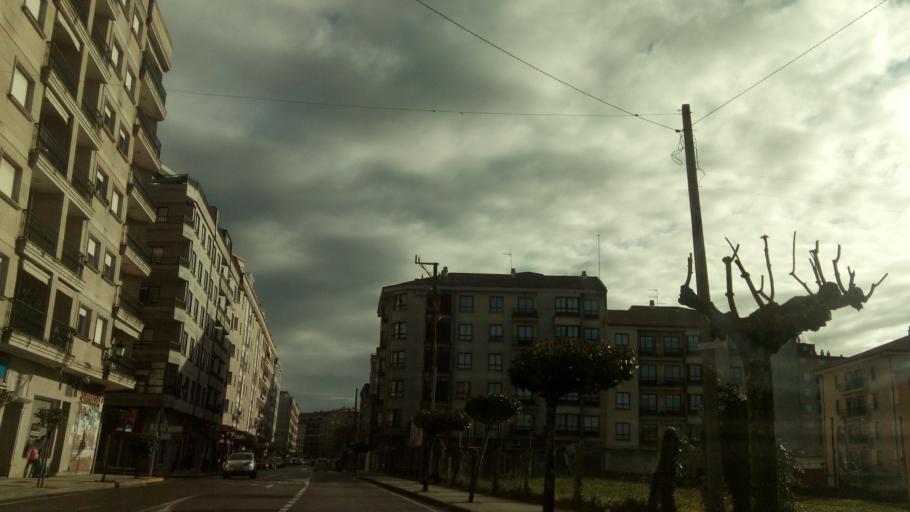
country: ES
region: Galicia
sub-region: Provincia de Pontevedra
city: Ponteareas
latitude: 42.1742
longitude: -8.5092
